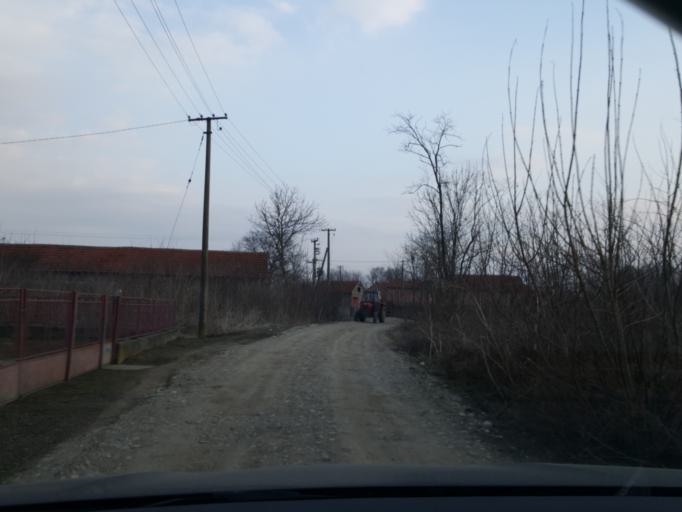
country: RS
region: Central Serbia
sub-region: Nisavski Okrug
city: Razanj
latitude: 43.5888
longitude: 21.6135
